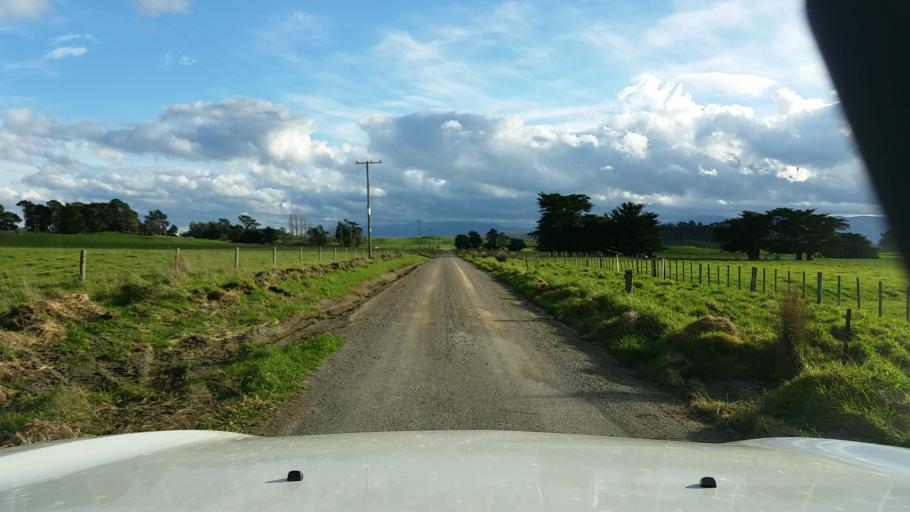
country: NZ
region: Wellington
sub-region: South Wairarapa District
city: Waipawa
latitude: -41.1999
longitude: 175.3620
